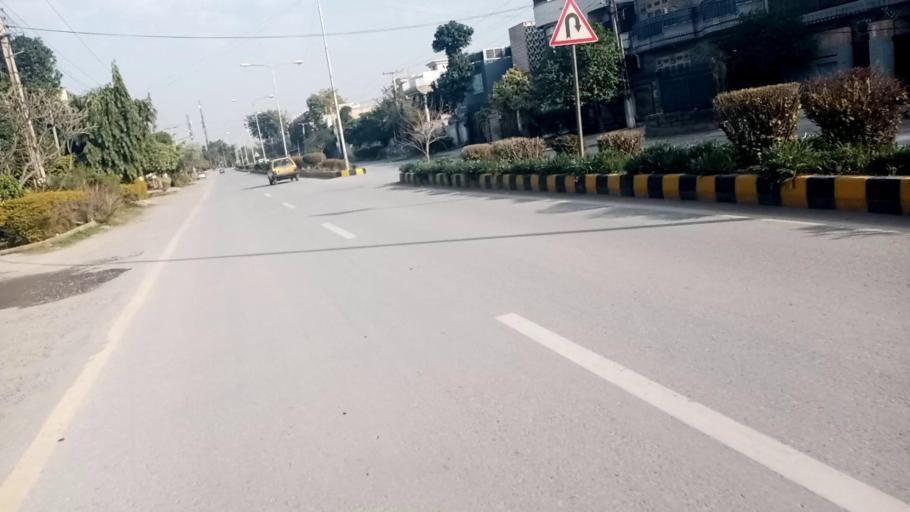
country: PK
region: Khyber Pakhtunkhwa
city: Peshawar
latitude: 33.9890
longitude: 71.4478
